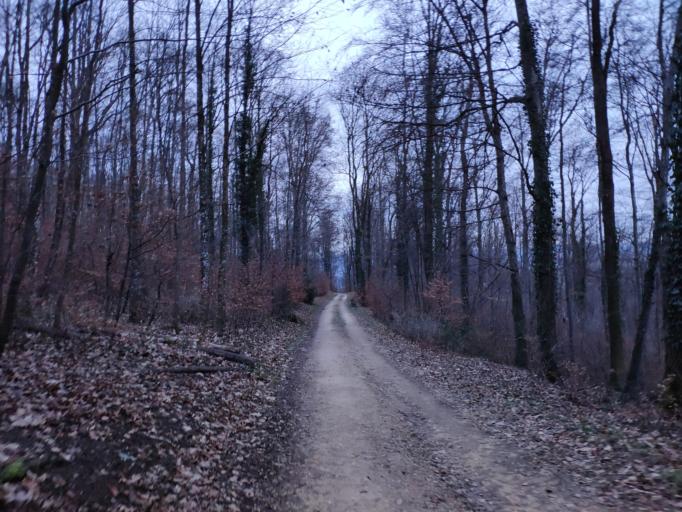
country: DE
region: Baden-Wuerttemberg
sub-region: Freiburg Region
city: Inzlingen
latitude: 47.5948
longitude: 7.6773
